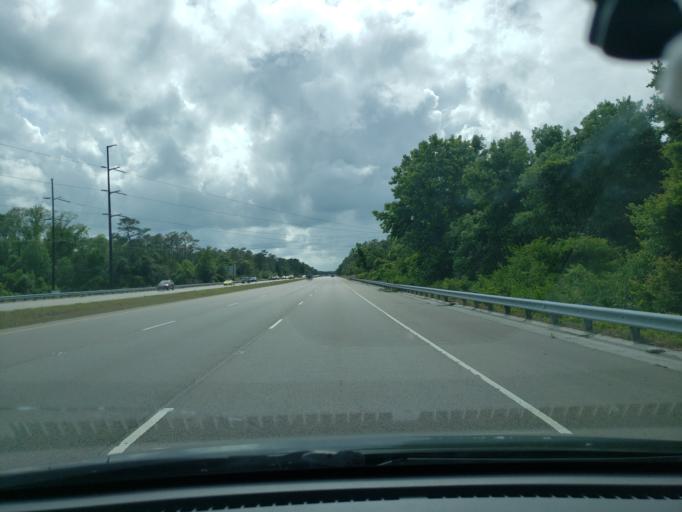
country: US
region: North Carolina
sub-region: New Hanover County
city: Kings Grant
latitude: 34.2550
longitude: -77.8786
